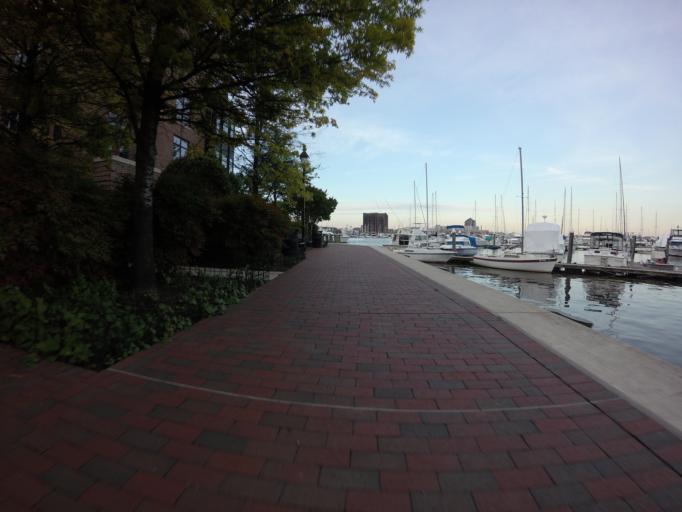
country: US
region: Maryland
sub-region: City of Baltimore
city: Baltimore
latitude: 39.2805
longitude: -76.5874
